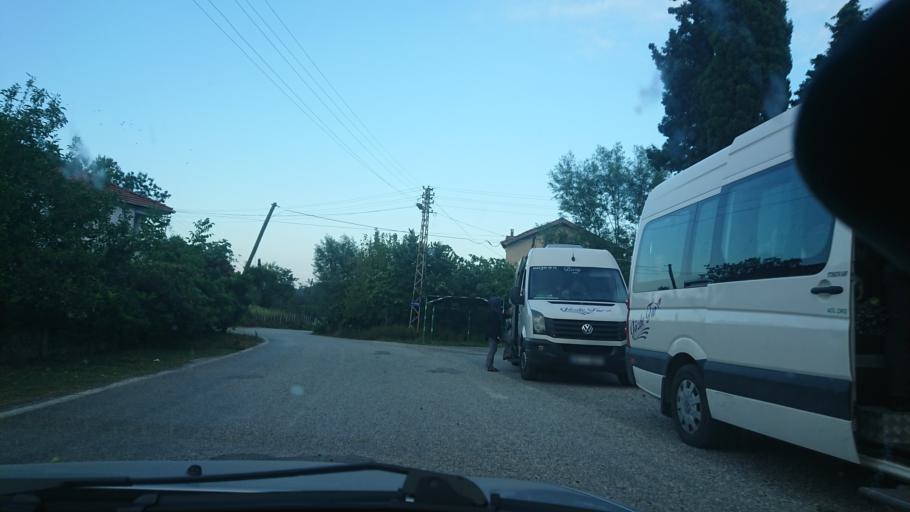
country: TR
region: Samsun
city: Tekkekoy
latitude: 41.1727
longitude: 36.5394
